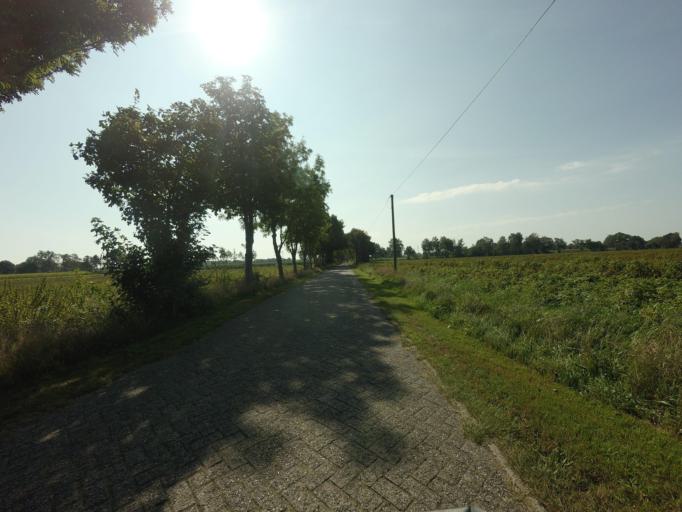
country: DE
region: Lower Saxony
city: Emlichheim
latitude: 52.5811
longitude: 6.8344
